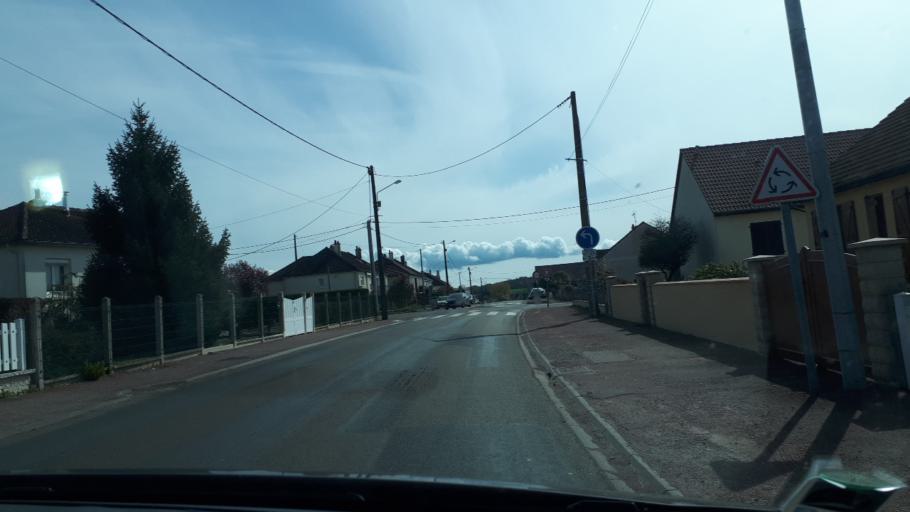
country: FR
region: Pays de la Loire
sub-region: Departement de la Sarthe
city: Yvre-le-Polin
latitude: 47.8192
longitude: 0.1446
